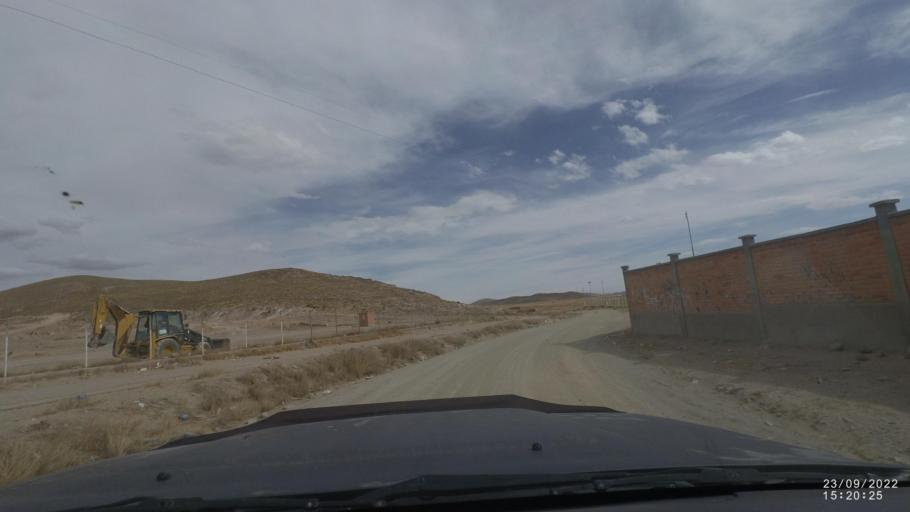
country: BO
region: Oruro
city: Oruro
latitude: -17.8966
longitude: -67.0448
